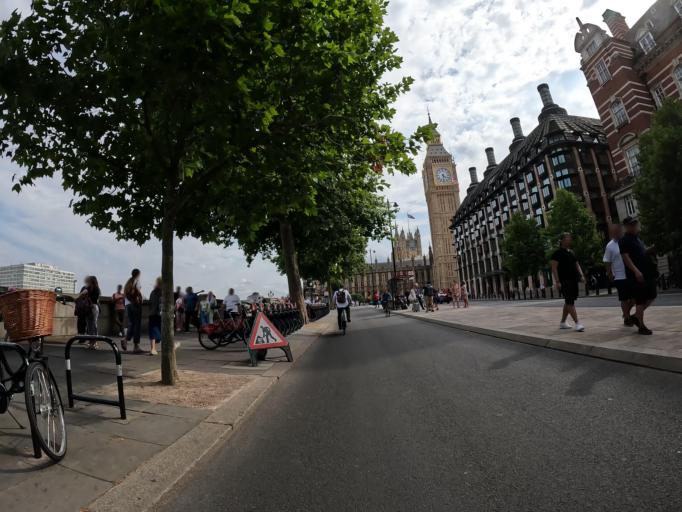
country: GB
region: England
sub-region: Greater London
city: Orpington
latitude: 51.3605
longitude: 0.0549
